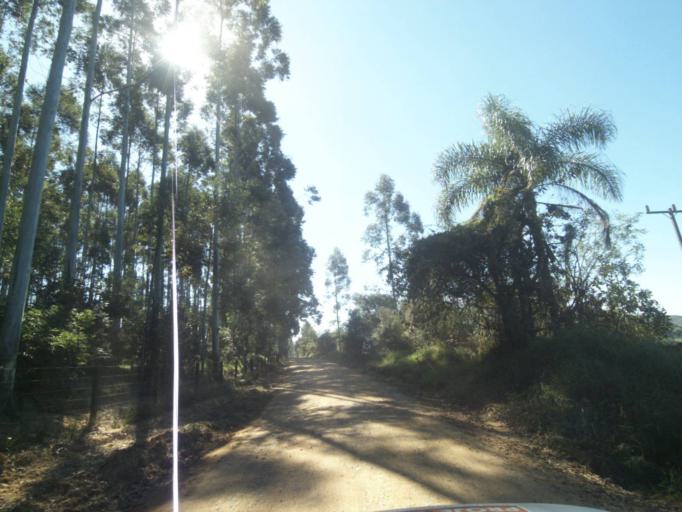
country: BR
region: Parana
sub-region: Tibagi
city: Tibagi
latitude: -24.5512
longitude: -50.6210
